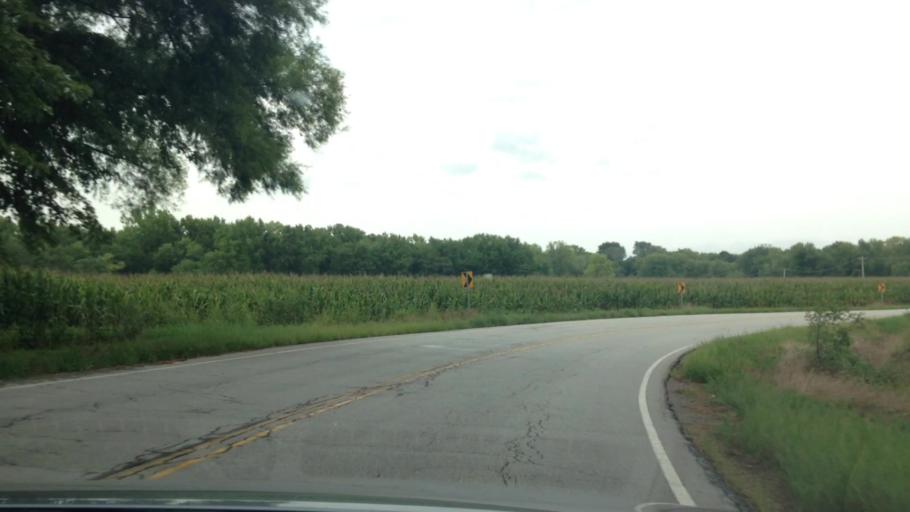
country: US
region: Missouri
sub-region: Clay County
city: Smithville
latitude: 39.4039
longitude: -94.6617
